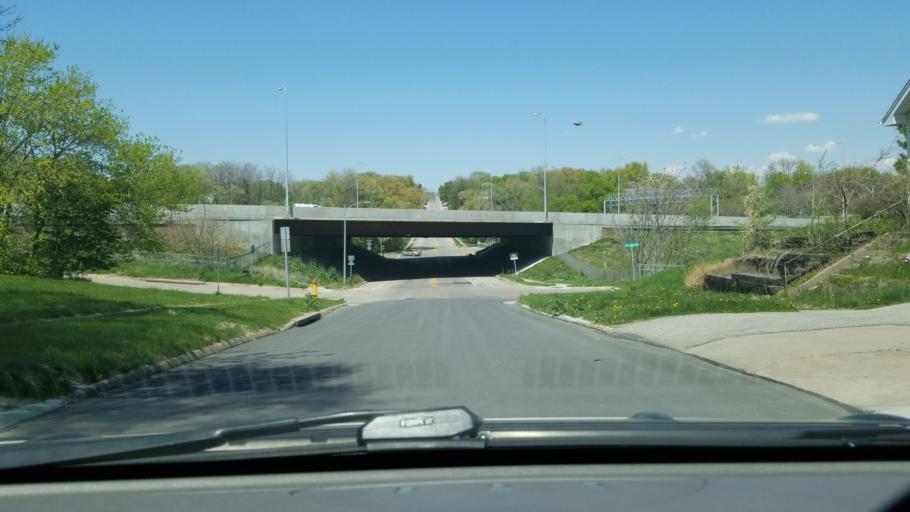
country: US
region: Nebraska
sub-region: Douglas County
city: Omaha
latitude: 41.2270
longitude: -95.9374
